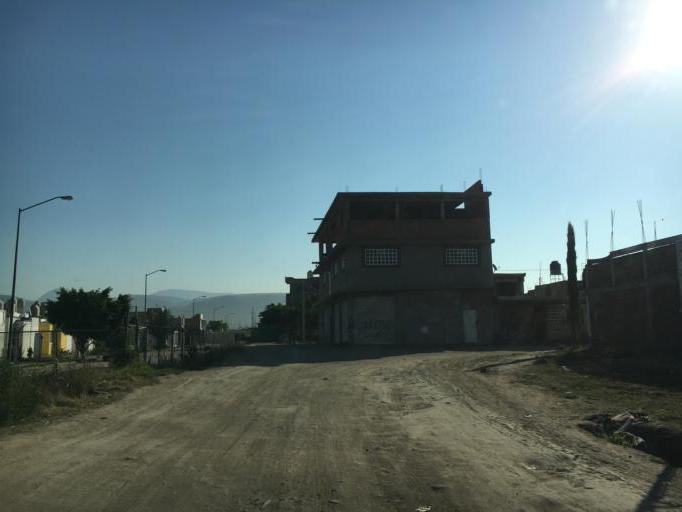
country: MX
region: Guanajuato
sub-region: Leon
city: Fraccionamiento Paraiso Real
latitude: 21.1038
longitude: -101.5978
